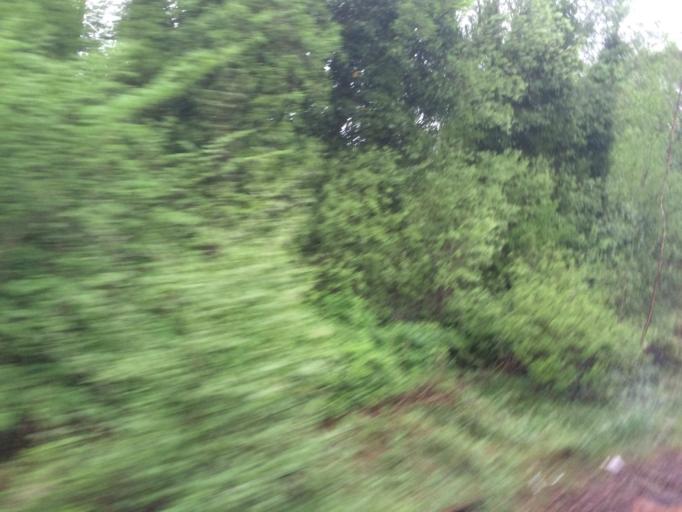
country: GB
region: Scotland
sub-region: Stirling
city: Dunblane
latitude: 56.1881
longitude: -3.9672
